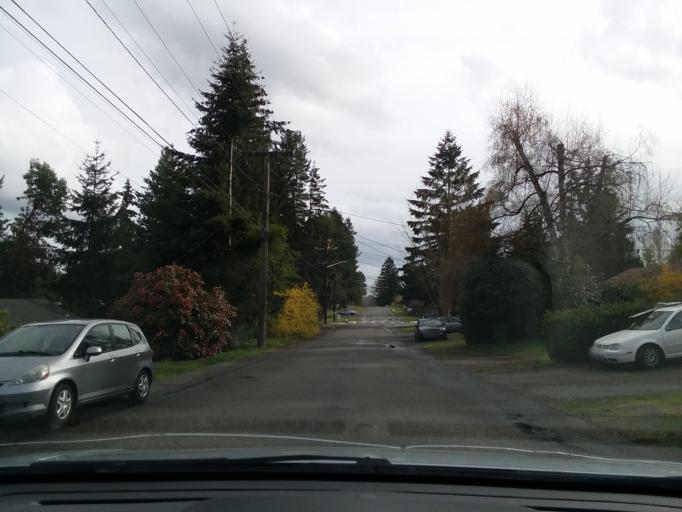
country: US
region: Washington
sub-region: Snohomish County
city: Mountlake Terrace
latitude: 47.7856
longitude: -122.3030
